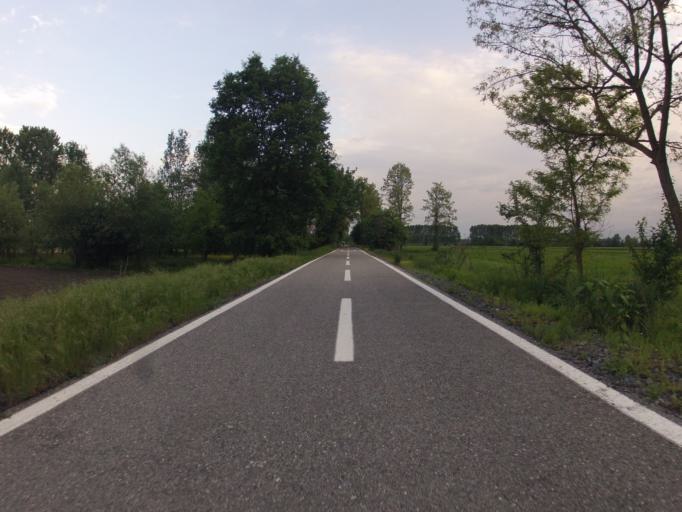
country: IT
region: Piedmont
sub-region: Provincia di Torino
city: Vigone
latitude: 44.8318
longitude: 7.4929
